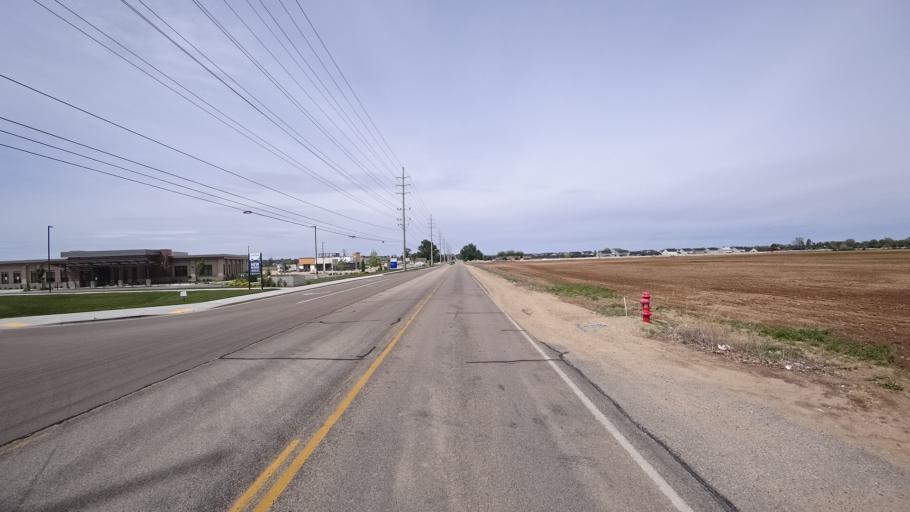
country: US
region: Idaho
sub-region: Ada County
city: Meridian
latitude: 43.5612
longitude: -116.3445
